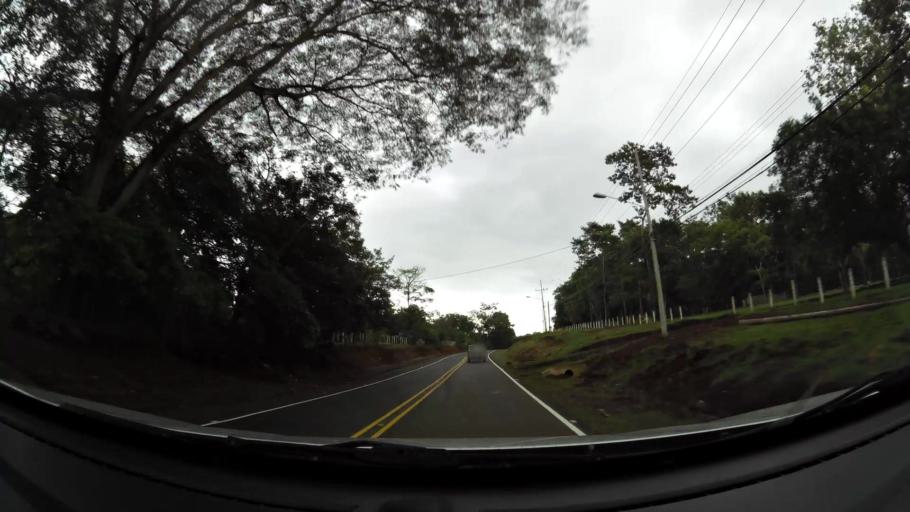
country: CR
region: Alajuela
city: Orotina
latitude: 9.9459
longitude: -84.5553
